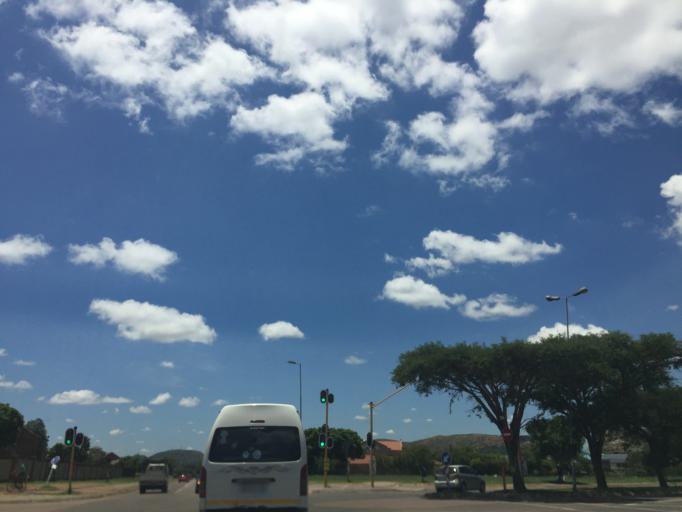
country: ZA
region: Gauteng
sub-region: City of Tshwane Metropolitan Municipality
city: Pretoria
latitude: -25.6644
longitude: 28.1077
